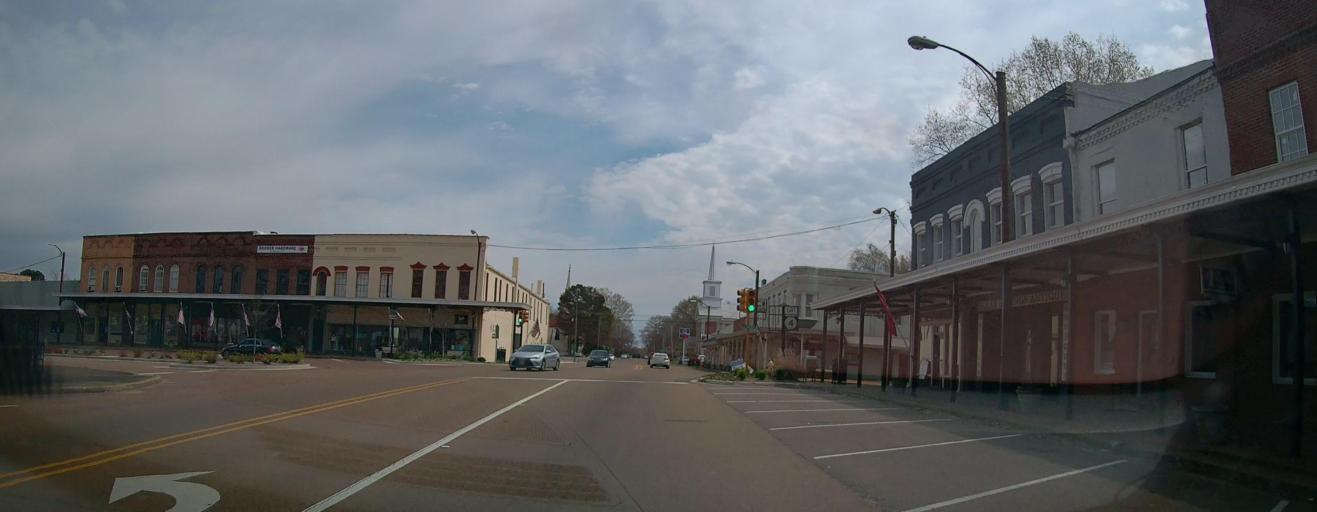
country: US
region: Mississippi
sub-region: Marshall County
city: Holly Springs
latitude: 34.7675
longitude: -89.4478
